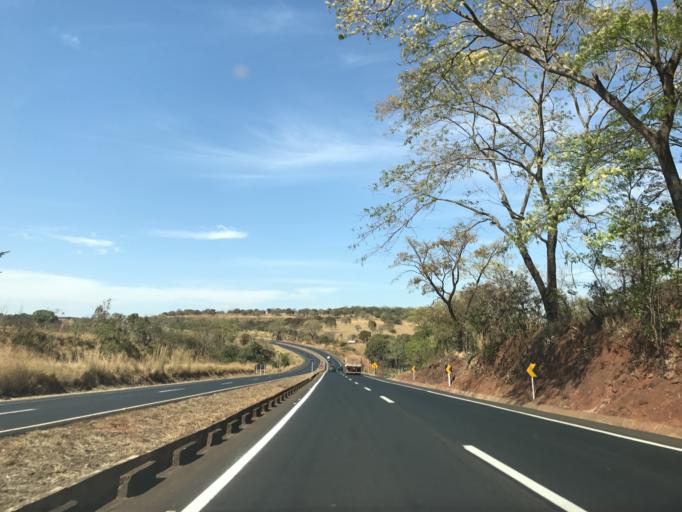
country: BR
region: Minas Gerais
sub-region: Monte Alegre De Minas
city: Monte Alegre de Minas
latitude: -18.7879
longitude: -49.0841
